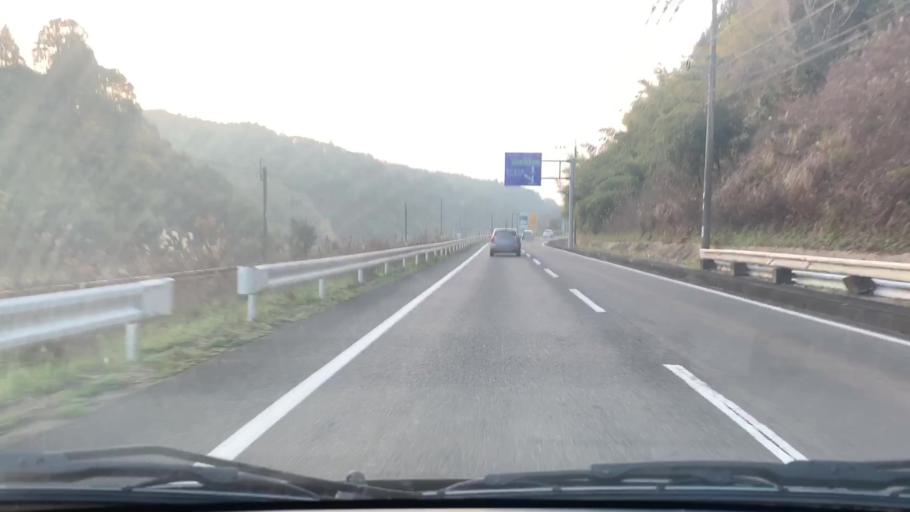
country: JP
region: Saga Prefecture
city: Imaricho-ko
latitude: 33.2612
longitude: 129.9148
